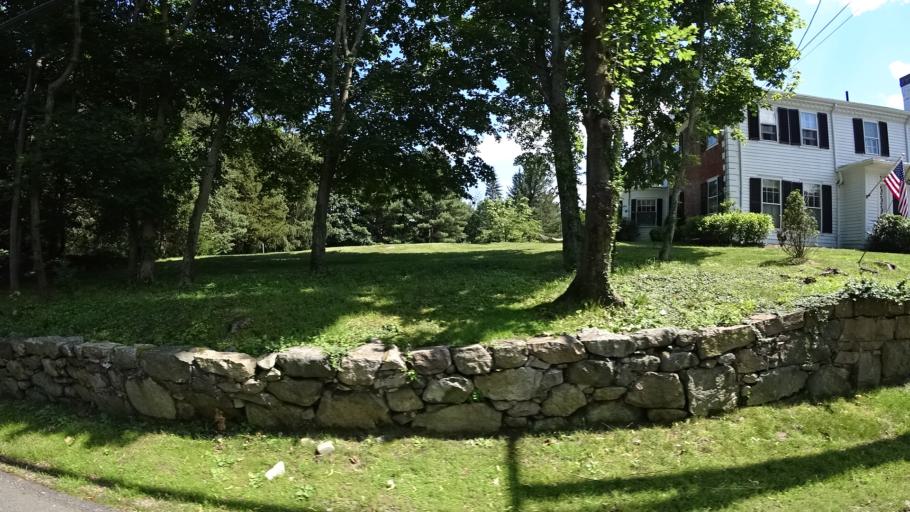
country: US
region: Massachusetts
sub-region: Norfolk County
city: Dedham
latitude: 42.2428
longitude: -71.1831
